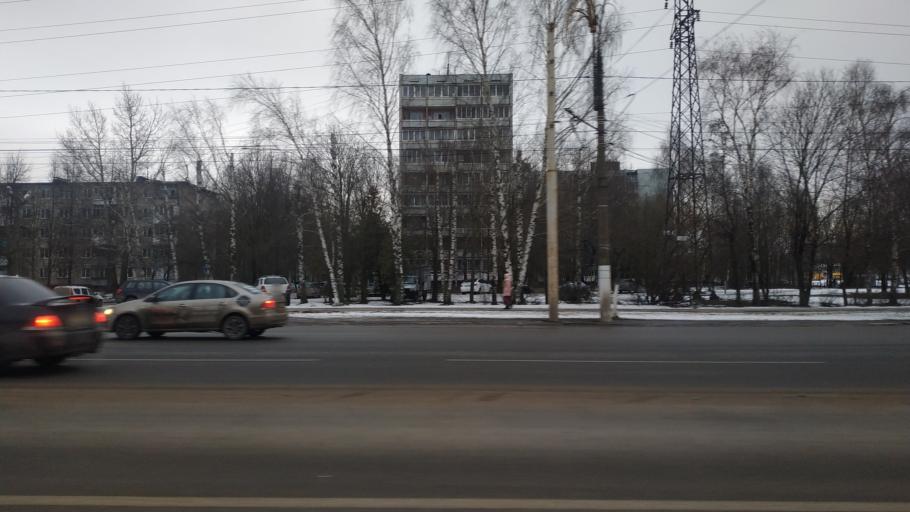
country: RU
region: Tverskaya
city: Tver
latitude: 56.8244
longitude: 35.8923
